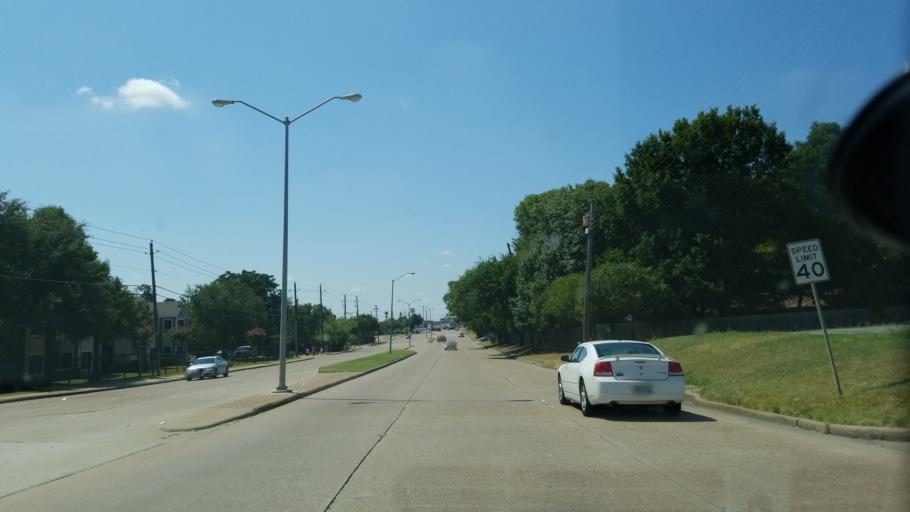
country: US
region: Texas
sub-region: Dallas County
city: Duncanville
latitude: 32.6656
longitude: -96.8916
